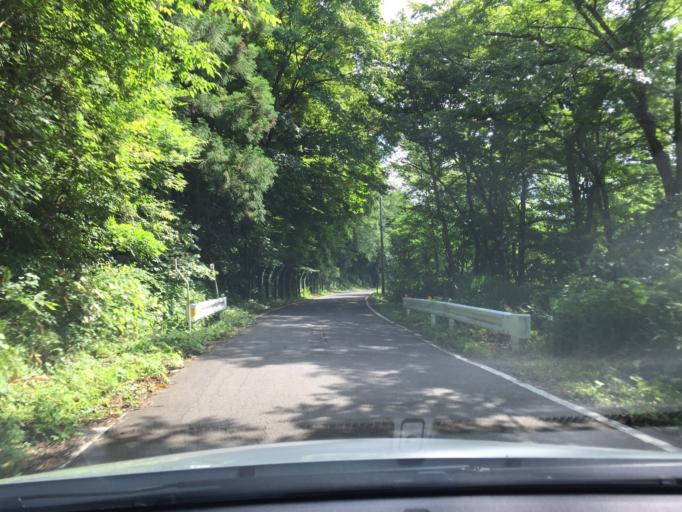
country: JP
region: Fukushima
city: Inawashiro
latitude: 37.2848
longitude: 140.0637
